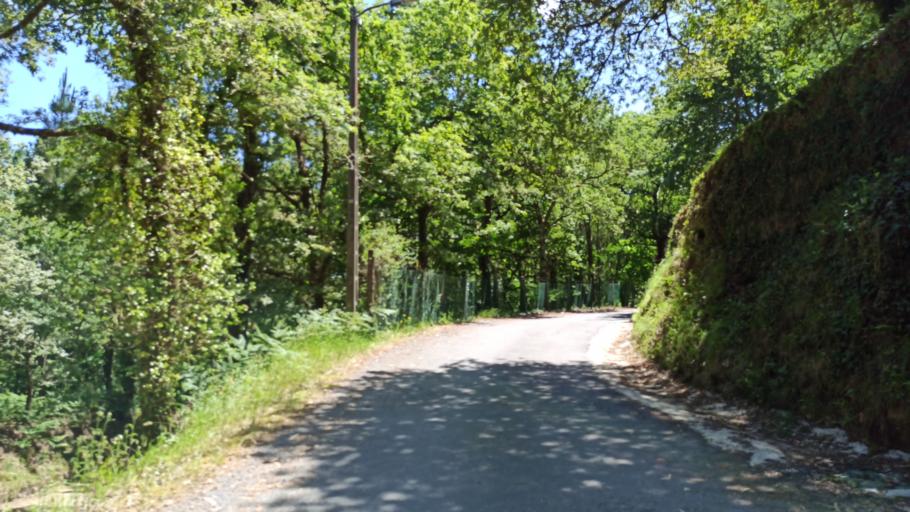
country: ES
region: Galicia
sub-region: Provincia da Coruna
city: Negreira
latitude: 42.9076
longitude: -8.7247
